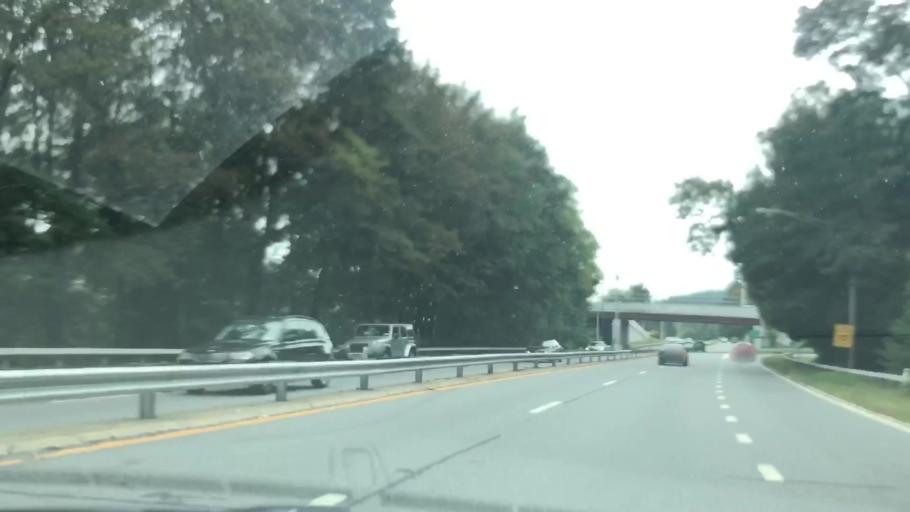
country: US
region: New York
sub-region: Westchester County
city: Ardsley
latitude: 41.0137
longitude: -73.8491
